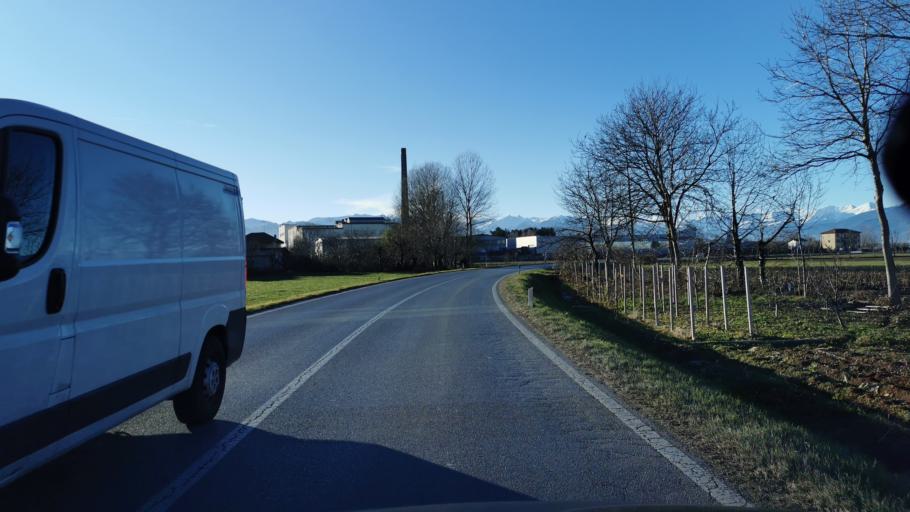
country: IT
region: Piedmont
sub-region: Provincia di Cuneo
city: Roata Rossi
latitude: 44.4261
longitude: 7.5500
